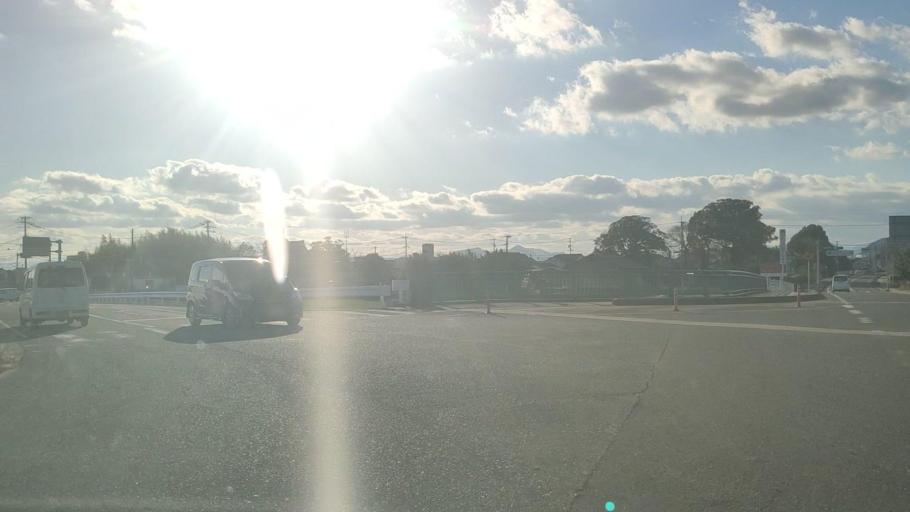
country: JP
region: Saga Prefecture
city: Saga-shi
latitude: 33.3087
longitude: 130.2597
